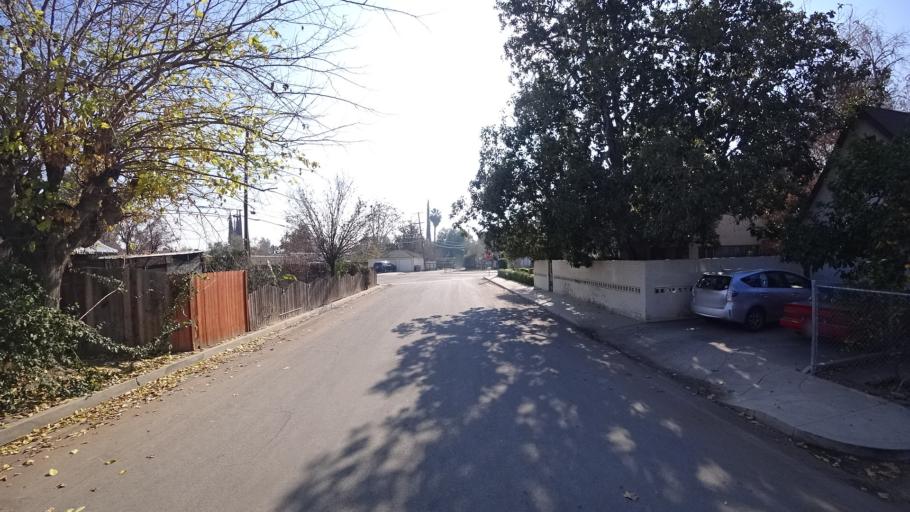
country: US
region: California
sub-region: Kern County
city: Bakersfield
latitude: 35.3862
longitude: -118.9972
